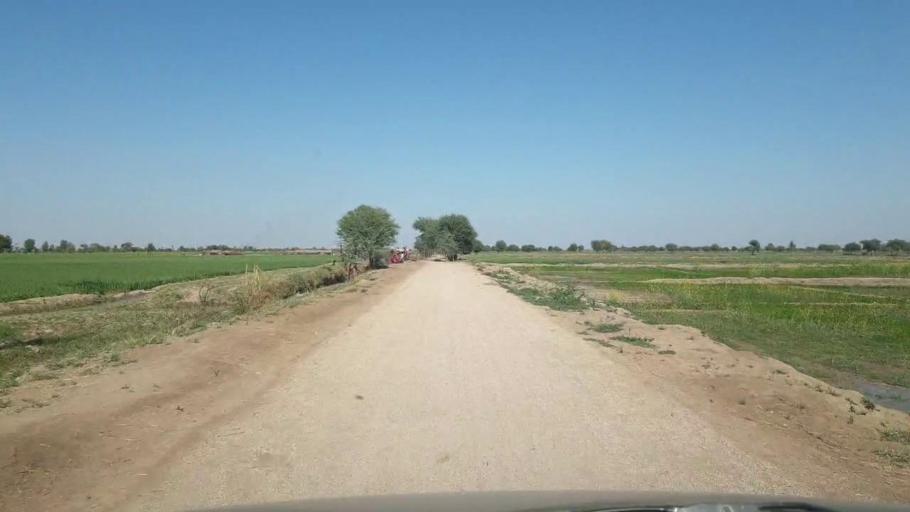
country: PK
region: Sindh
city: Dhoro Naro
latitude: 25.3803
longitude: 69.6012
